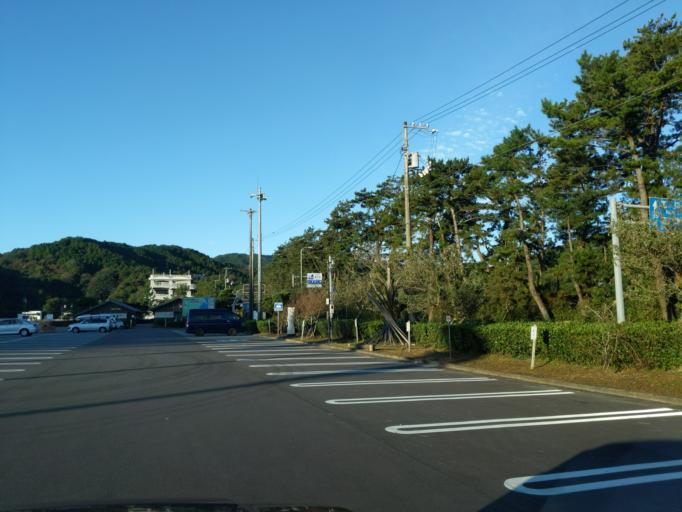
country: JP
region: Kochi
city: Muroto-misakicho
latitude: 33.5437
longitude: 134.2953
